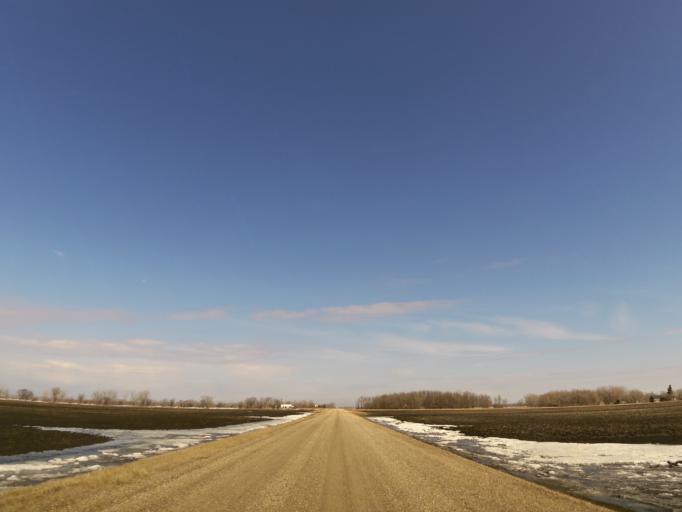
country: US
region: North Dakota
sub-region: Walsh County
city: Grafton
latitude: 48.3871
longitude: -97.1683
